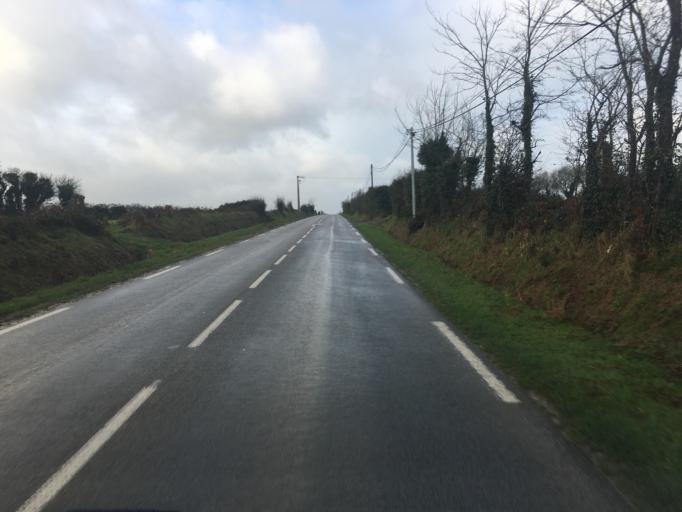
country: FR
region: Lower Normandy
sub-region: Departement de la Manche
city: Saint-Pierre-Eglise
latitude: 49.6704
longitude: -1.3476
